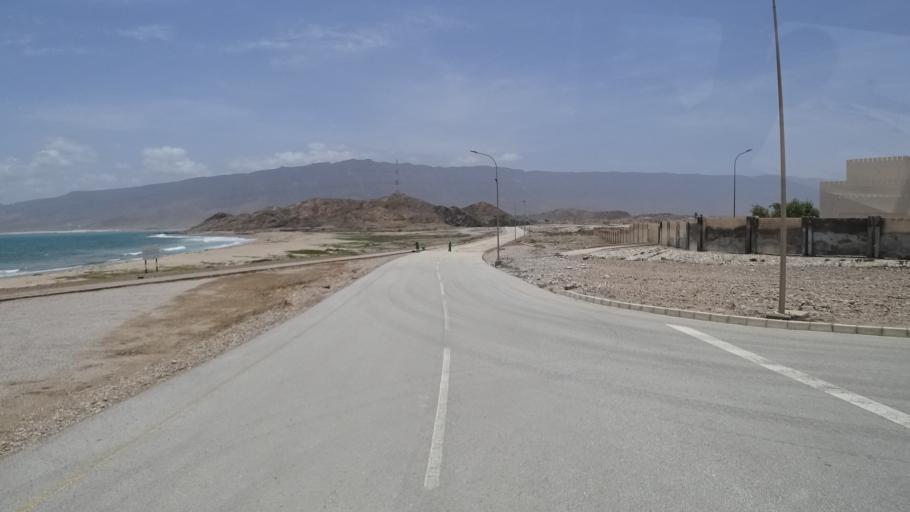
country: OM
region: Zufar
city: Salalah
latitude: 16.9928
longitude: 54.6916
